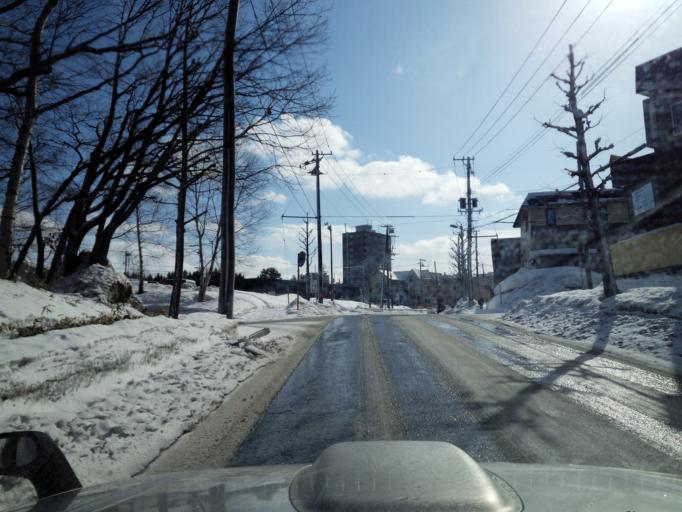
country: JP
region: Hokkaido
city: Kitahiroshima
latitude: 42.9867
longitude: 141.4439
